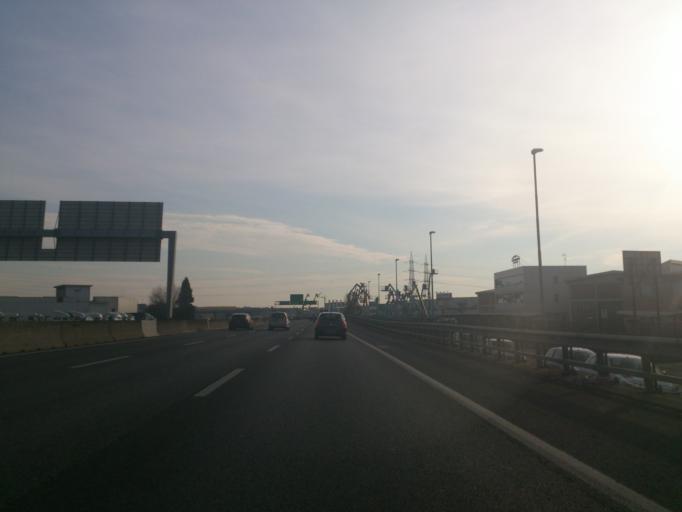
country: IT
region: Lombardy
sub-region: Citta metropolitana di Milano
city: Civesio
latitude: 45.3974
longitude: 9.2604
